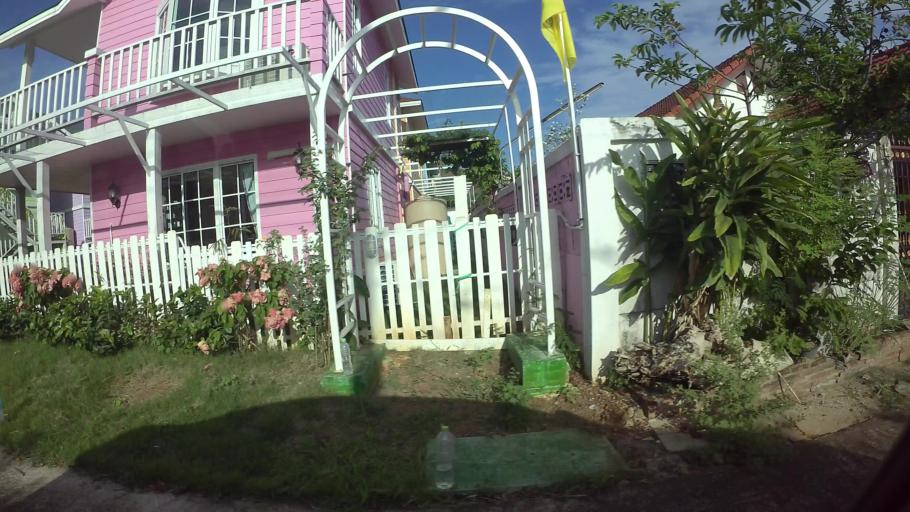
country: TH
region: Chon Buri
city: Sattahip
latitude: 12.6765
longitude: 100.9176
